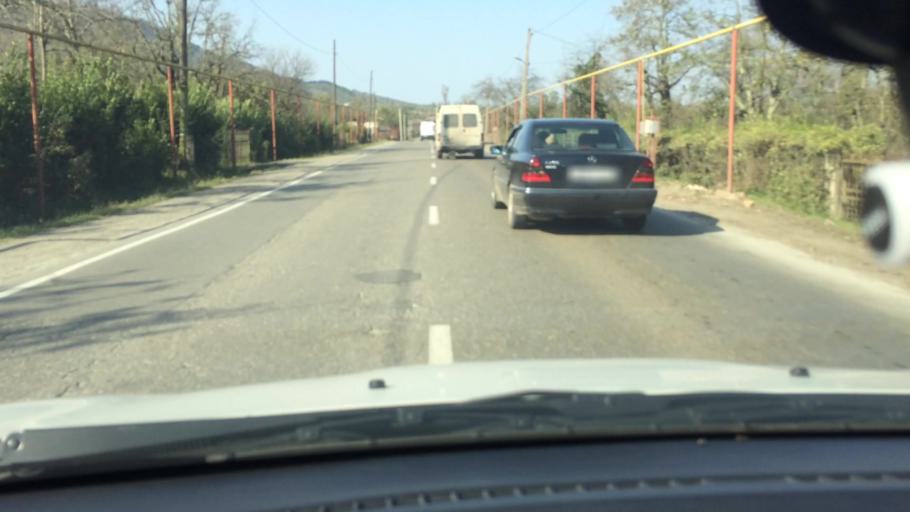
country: GE
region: Guria
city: Lanchkhuti
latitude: 42.0750
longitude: 42.0728
